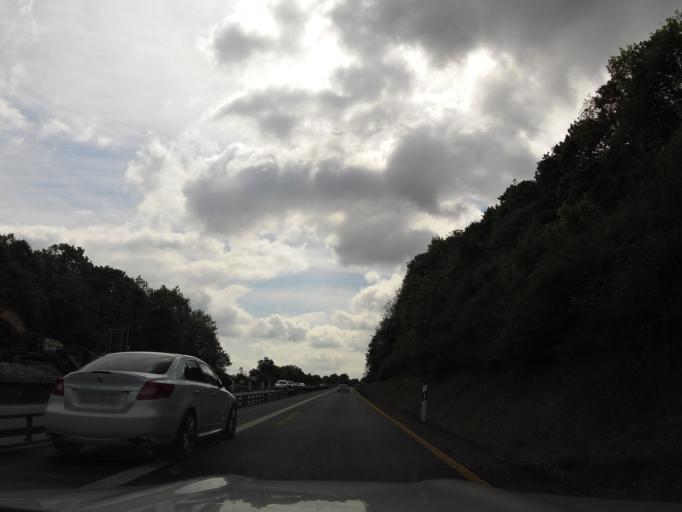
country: DE
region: Hesse
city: Allendorf an der Lahn
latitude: 50.5441
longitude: 8.5737
